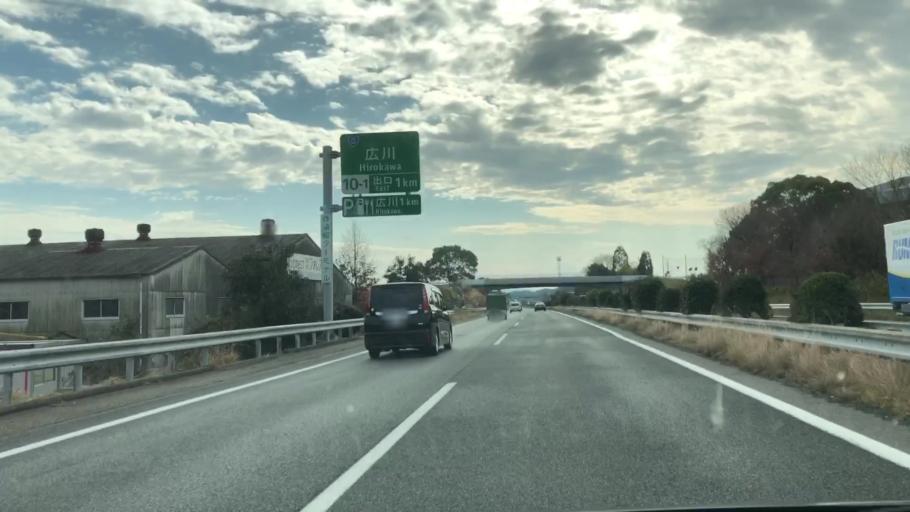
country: JP
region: Fukuoka
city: Kurume
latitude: 33.2661
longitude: 130.5390
